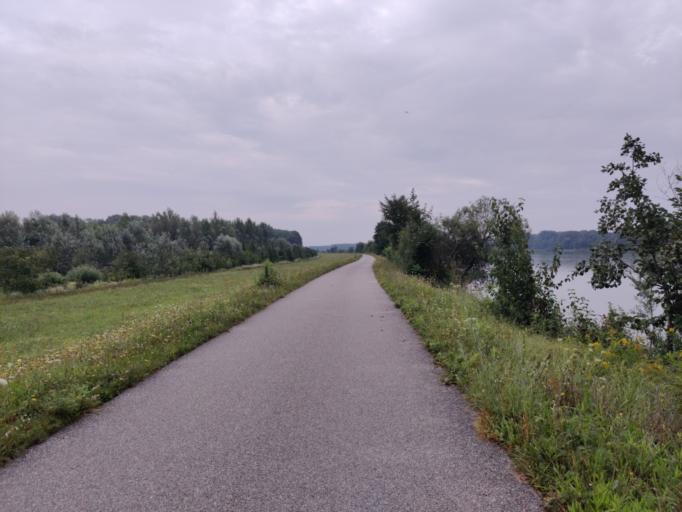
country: AT
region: Upper Austria
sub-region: Politischer Bezirk Urfahr-Umgebung
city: Steyregg
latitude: 48.2677
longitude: 14.3874
